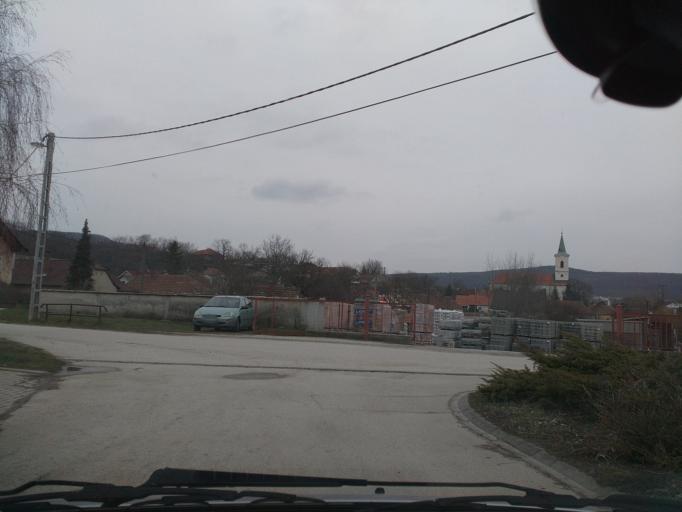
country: HU
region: Komarom-Esztergom
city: Piliscsev
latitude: 47.6811
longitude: 18.8195
